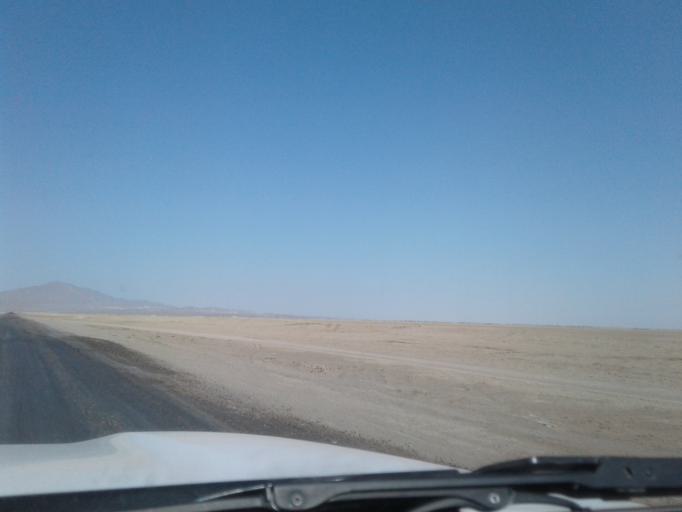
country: TM
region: Balkan
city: Gumdag
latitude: 39.2204
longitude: 54.6576
